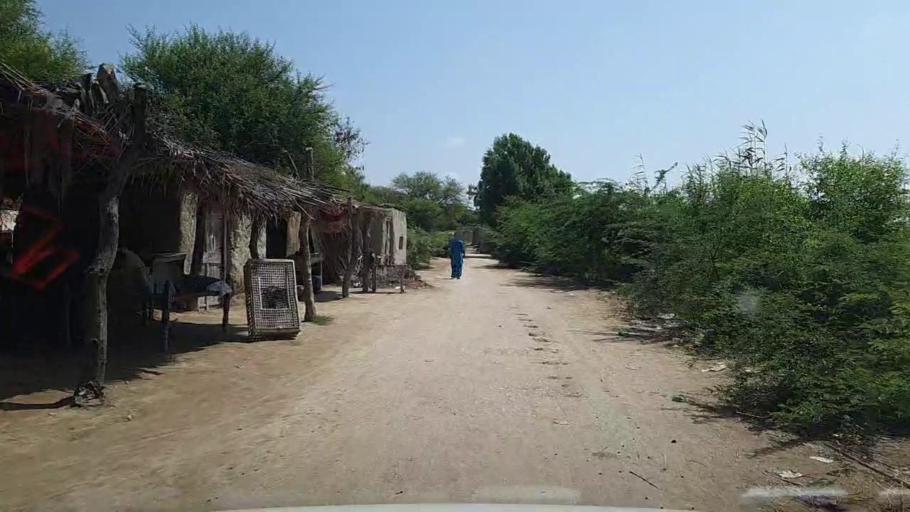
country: PK
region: Sindh
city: Kario
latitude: 24.8447
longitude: 68.6981
